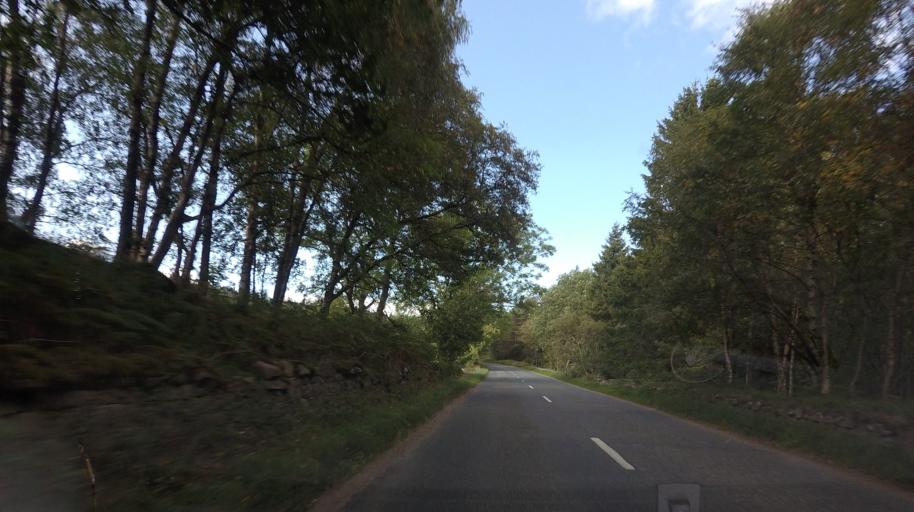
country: GB
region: Scotland
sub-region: Aberdeenshire
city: Banchory
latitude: 57.1159
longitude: -2.4260
